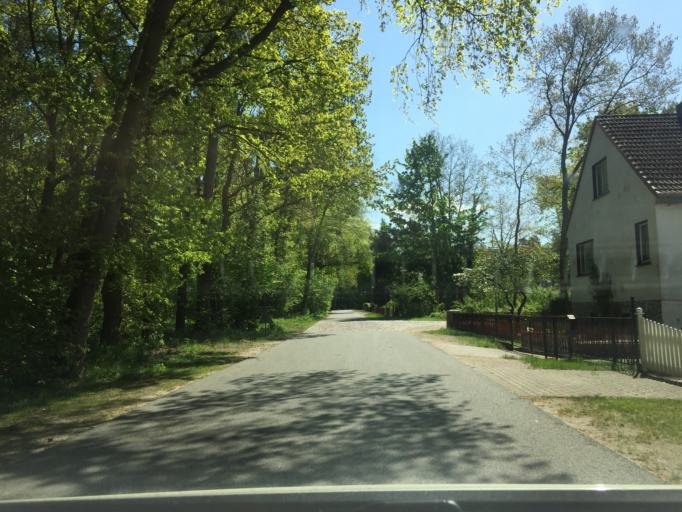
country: DE
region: Mecklenburg-Vorpommern
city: Torgelow
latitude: 53.6366
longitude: 14.0361
